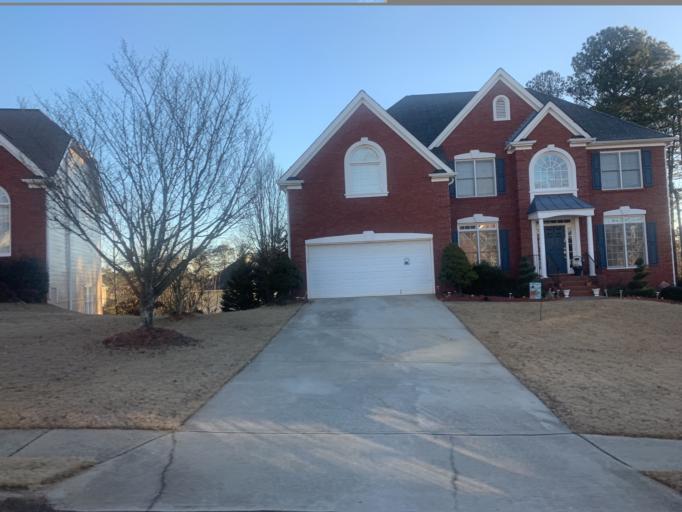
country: US
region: Georgia
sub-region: Gwinnett County
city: Mountain Park
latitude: 33.8708
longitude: -84.1093
